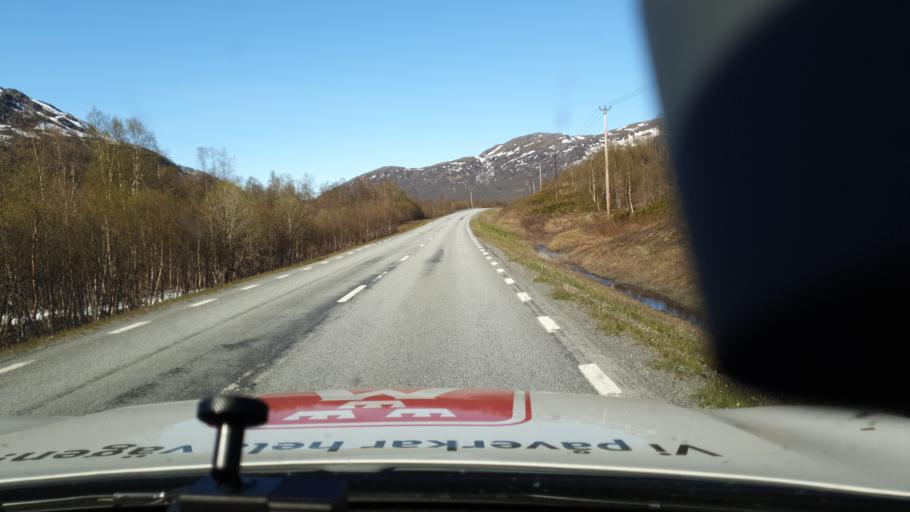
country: NO
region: Nordland
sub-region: Rana
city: Mo i Rana
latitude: 65.9235
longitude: 15.0068
